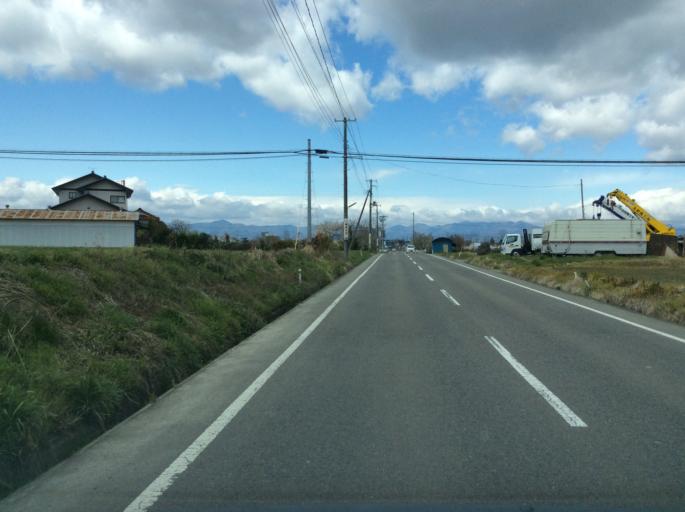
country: JP
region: Fukushima
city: Koriyama
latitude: 37.3553
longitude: 140.4011
